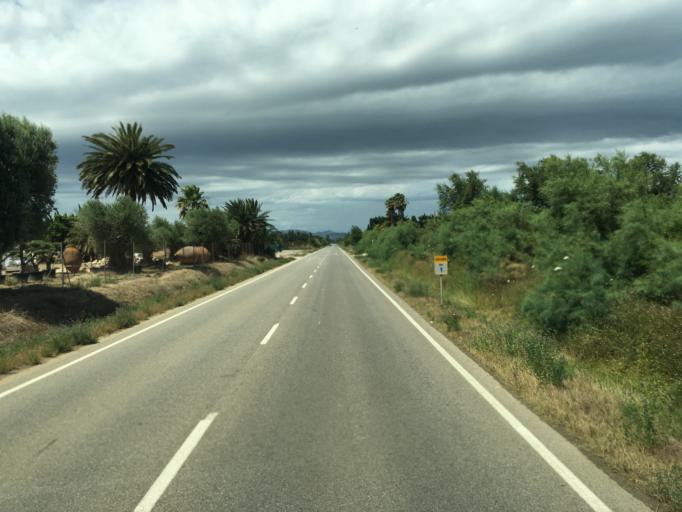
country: ES
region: Catalonia
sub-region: Provincia de Girona
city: Sant Pere Pescador
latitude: 42.2003
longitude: 3.0838
